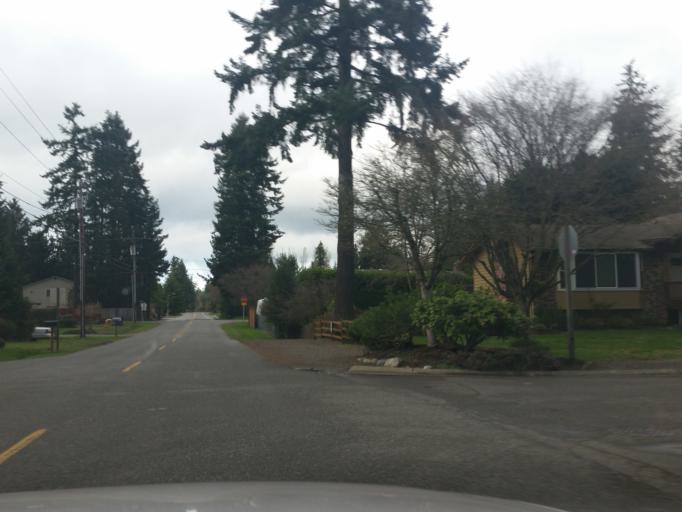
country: US
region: Washington
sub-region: Snohomish County
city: Meadowdale
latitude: 47.8599
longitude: -122.3091
